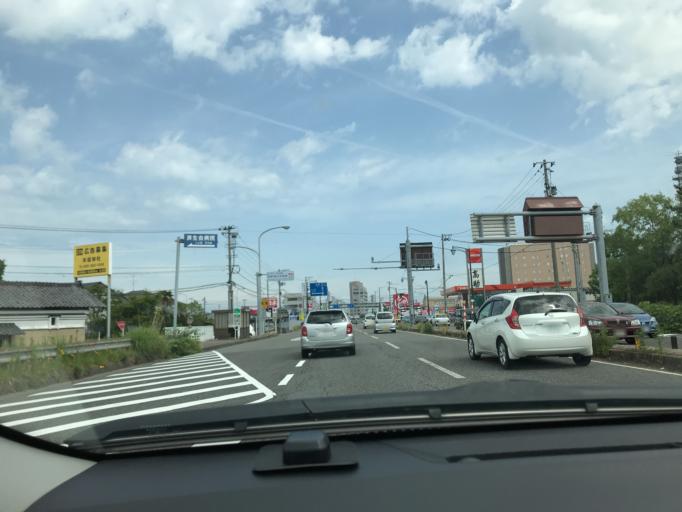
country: JP
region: Niigata
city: Niigata-shi
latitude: 37.8788
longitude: 139.0139
